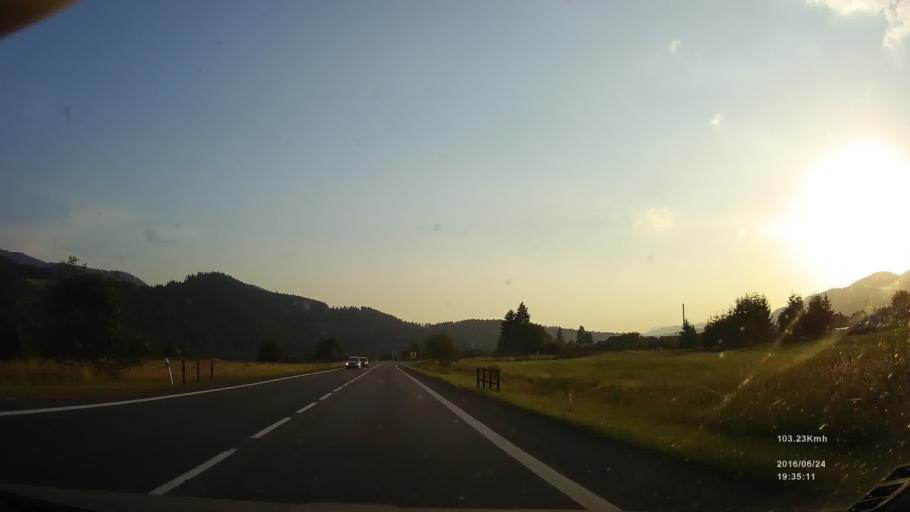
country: SK
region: Banskobystricky
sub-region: Okres Banska Bystrica
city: Brezno
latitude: 48.8105
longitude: 19.4658
